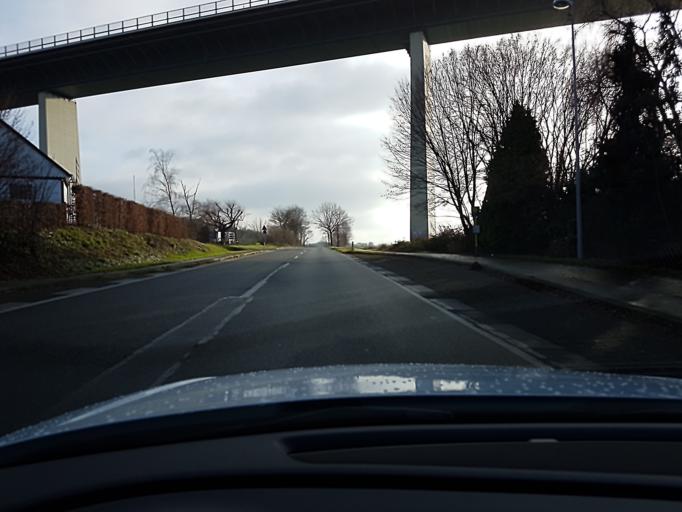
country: DE
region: North Rhine-Westphalia
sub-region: Regierungsbezirk Dusseldorf
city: Muelheim (Ruhr)
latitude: 51.3826
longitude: 6.9082
